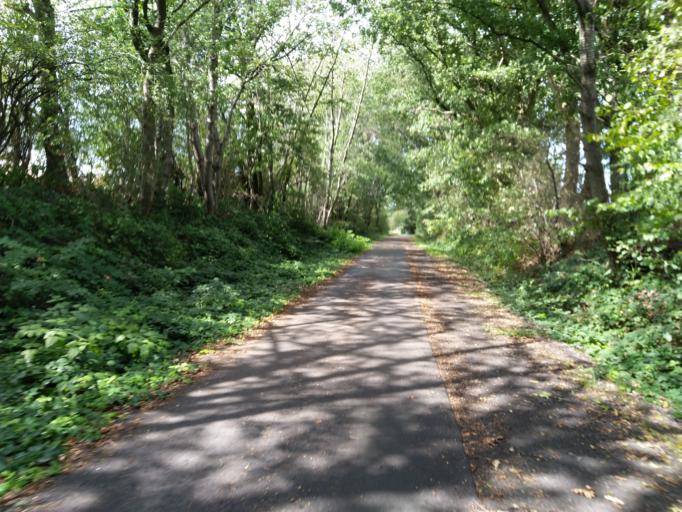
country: BE
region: Wallonia
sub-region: Province de Liege
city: Aubel
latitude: 50.6746
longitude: 5.8548
